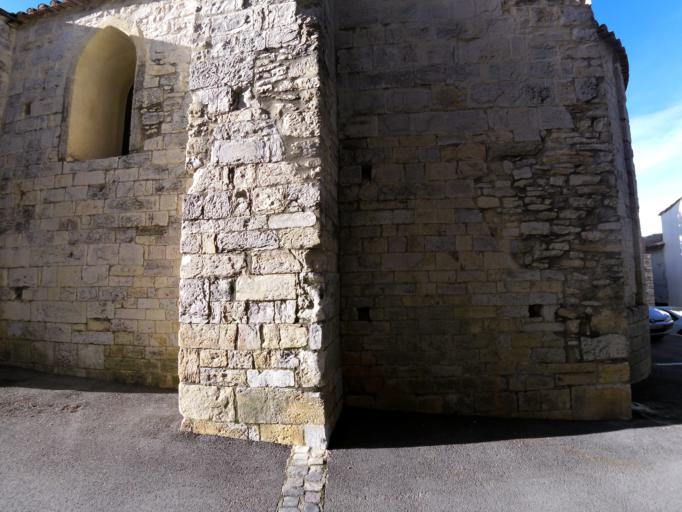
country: FR
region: Languedoc-Roussillon
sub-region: Departement du Gard
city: Langlade
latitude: 43.8038
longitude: 4.2495
